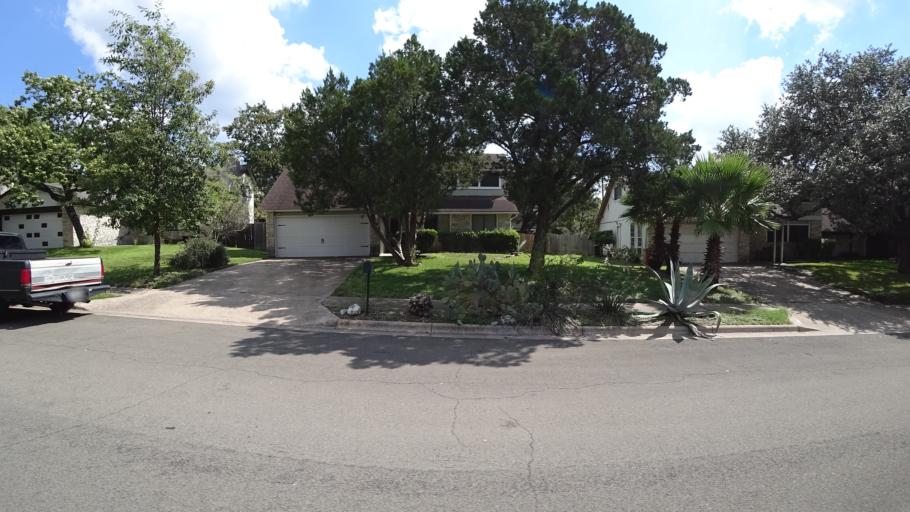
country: US
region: Texas
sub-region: Travis County
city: Onion Creek
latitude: 30.1910
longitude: -97.7881
